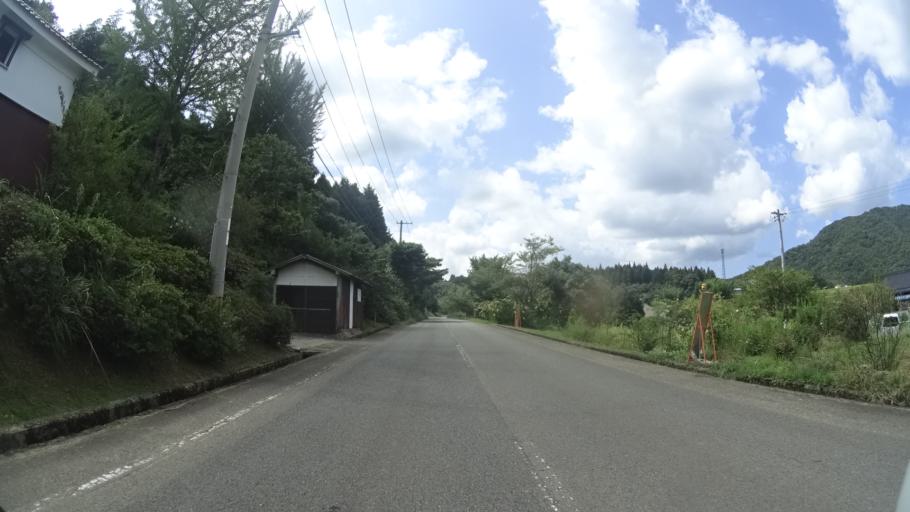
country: JP
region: Yamaguchi
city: Hagi
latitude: 34.5141
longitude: 131.5973
